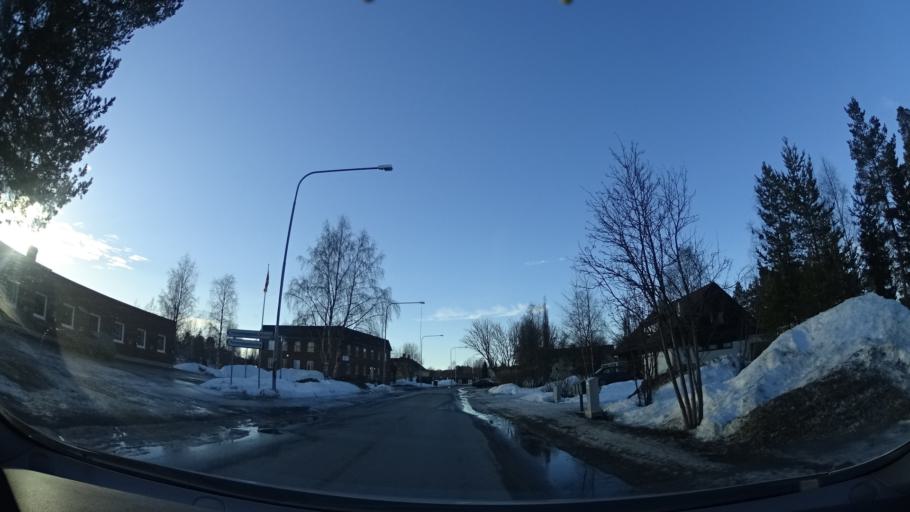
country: SE
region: Vaesterbotten
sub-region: Skelleftea Kommun
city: Byske
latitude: 64.9507
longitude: 21.2057
